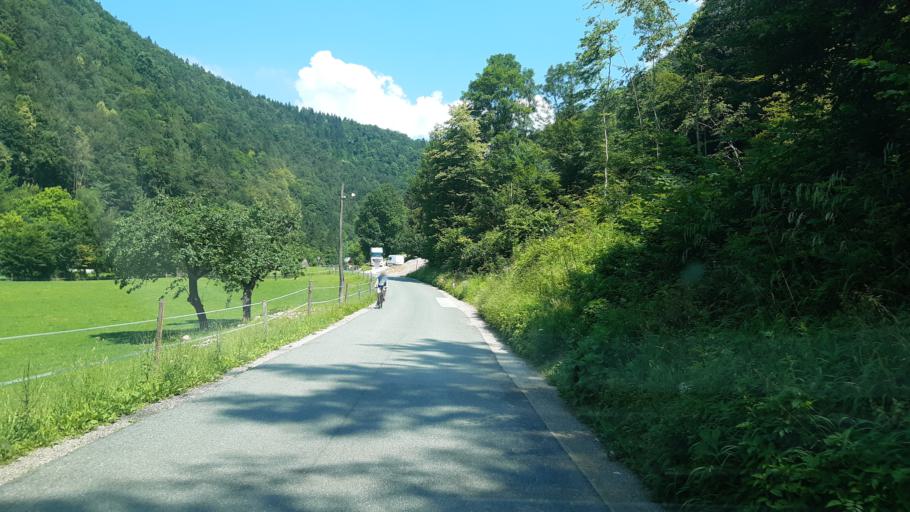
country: SI
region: Cerklje na Gorenjskem
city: Cerklje na Gorenjskem
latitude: 46.2660
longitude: 14.4940
